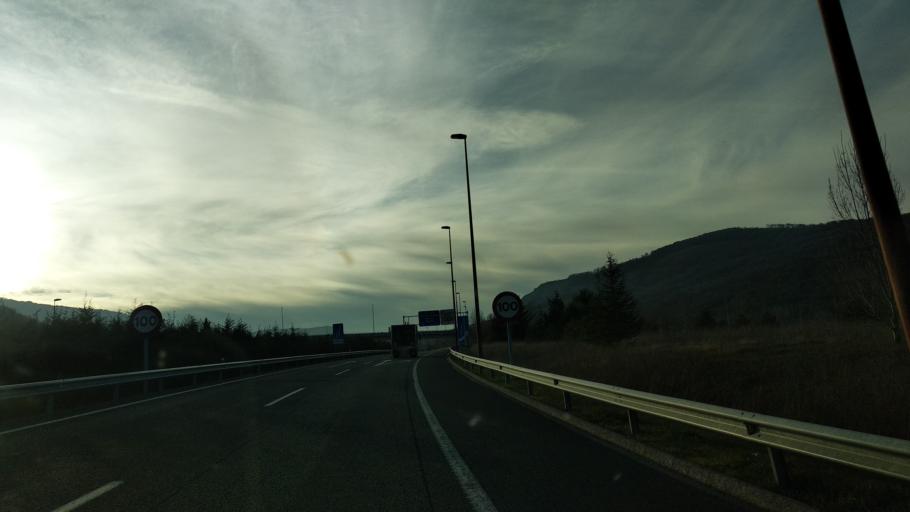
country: ES
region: Navarre
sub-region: Provincia de Navarra
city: Altsasu
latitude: 42.8867
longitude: -2.1744
